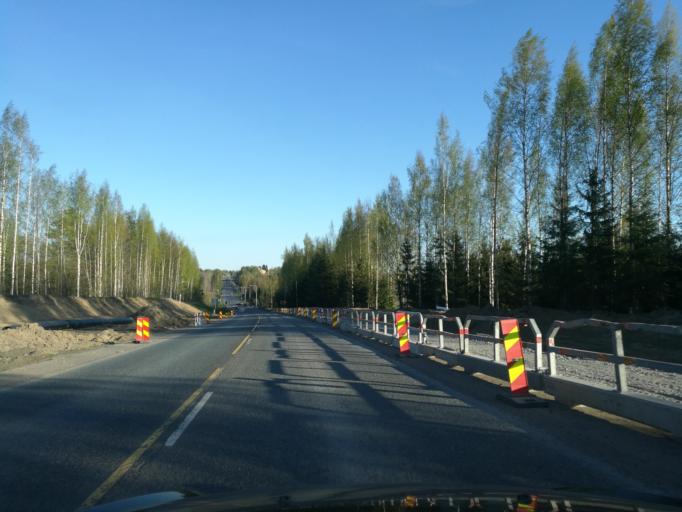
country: FI
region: Uusimaa
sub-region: Helsinki
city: Tuusula
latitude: 60.4038
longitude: 25.0090
